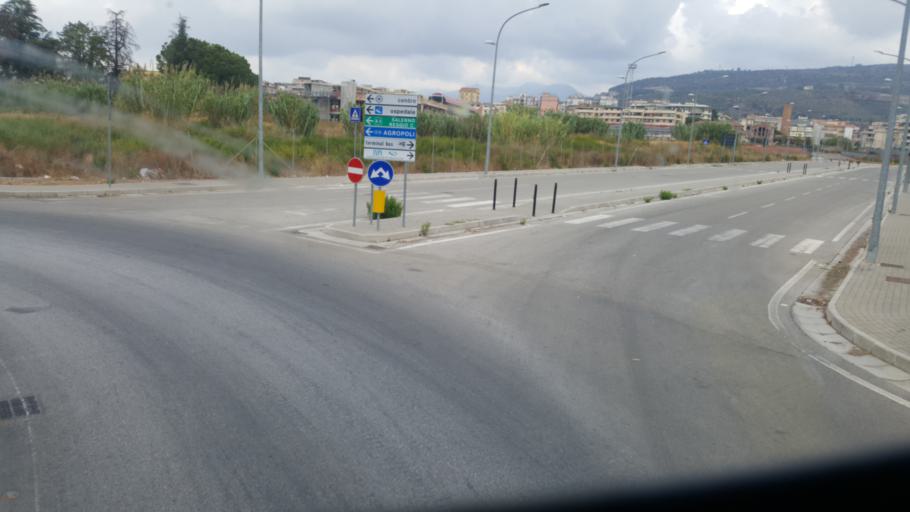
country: IT
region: Campania
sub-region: Provincia di Salerno
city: Battipaglia
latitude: 40.6024
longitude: 14.9841
